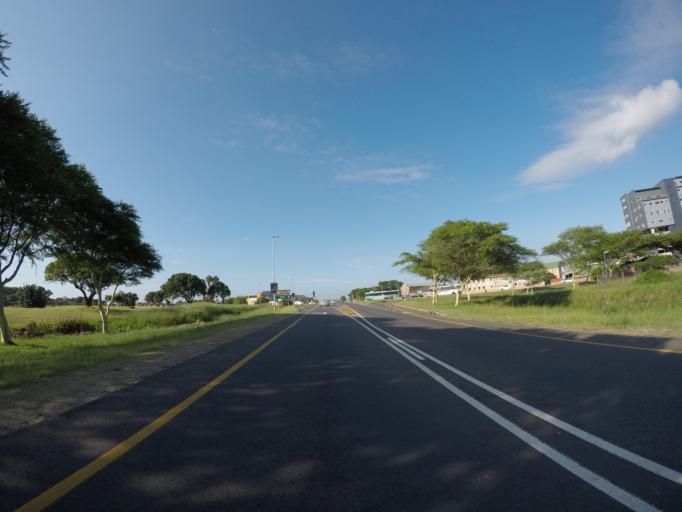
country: ZA
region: KwaZulu-Natal
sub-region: uThungulu District Municipality
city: Richards Bay
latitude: -28.7496
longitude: 32.0560
